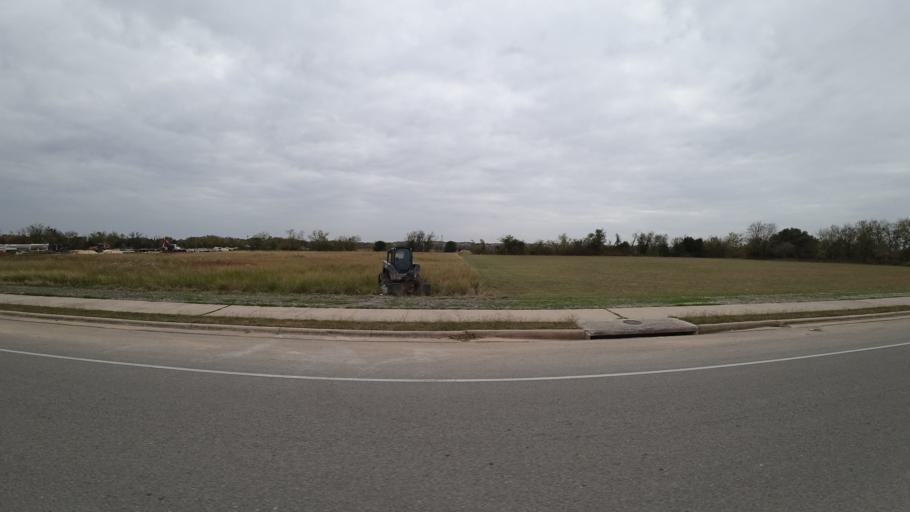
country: US
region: Texas
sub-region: Travis County
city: Pflugerville
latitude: 30.4568
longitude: -97.6242
